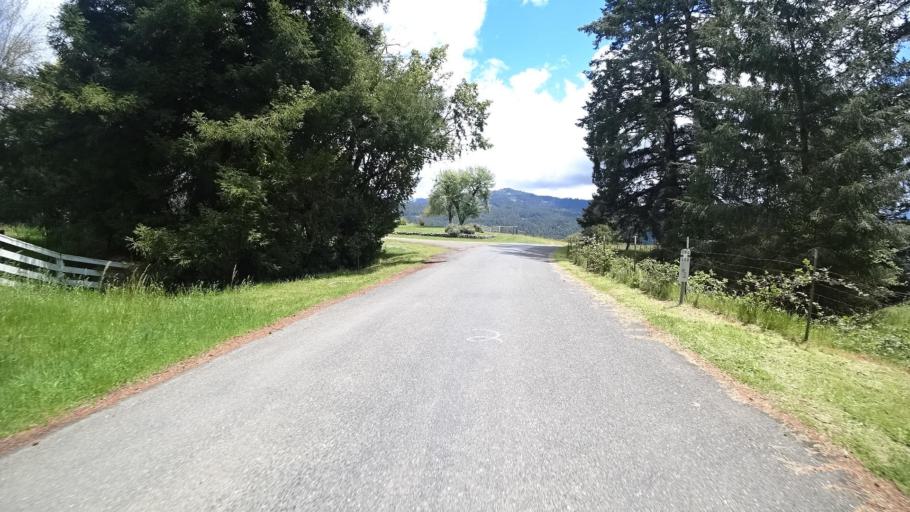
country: US
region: California
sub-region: Humboldt County
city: Blue Lake
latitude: 40.8448
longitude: -123.9116
